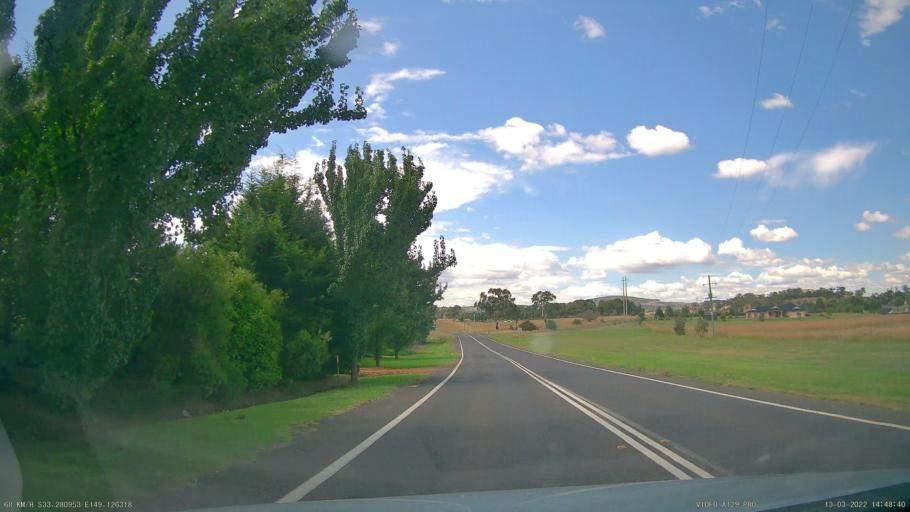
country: AU
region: New South Wales
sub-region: Orange Municipality
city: Orange
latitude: -33.2808
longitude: 149.1265
